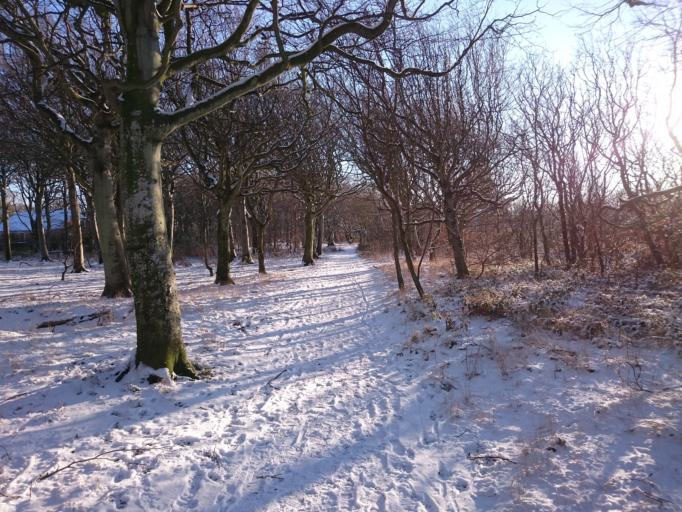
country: DK
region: North Denmark
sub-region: Frederikshavn Kommune
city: Skagen
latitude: 57.7188
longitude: 10.5703
